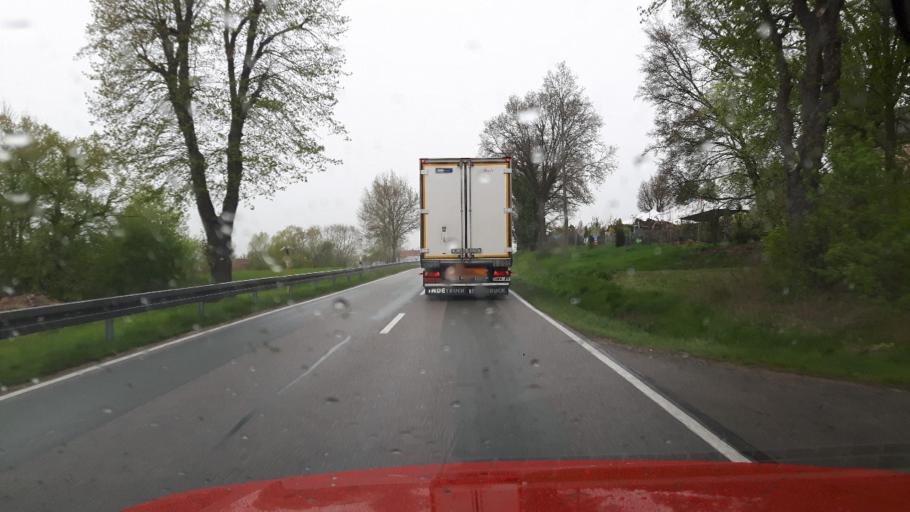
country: DE
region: Bavaria
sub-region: Regierungsbezirk Mittelfranken
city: Muhr am See
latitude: 49.1556
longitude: 10.7190
